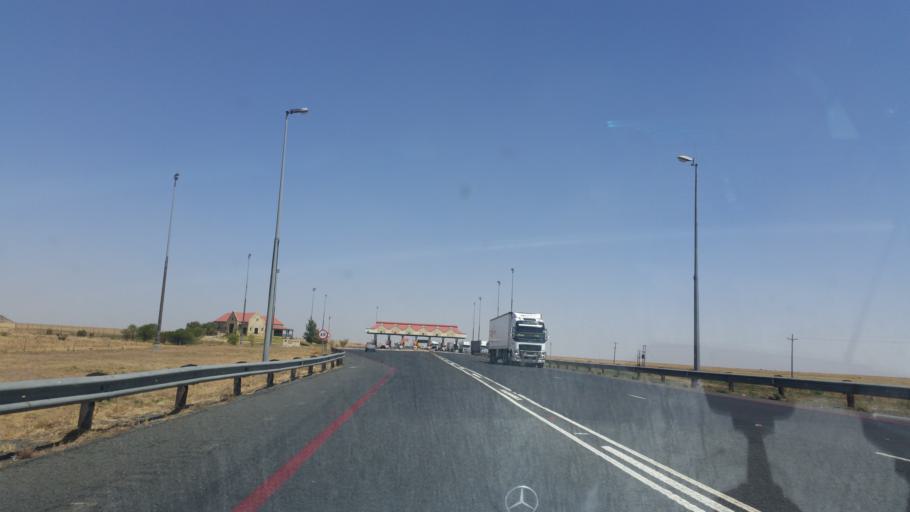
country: ZA
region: Orange Free State
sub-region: Lejweleputswa District Municipality
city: Brandfort
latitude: -28.7971
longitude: 26.6927
